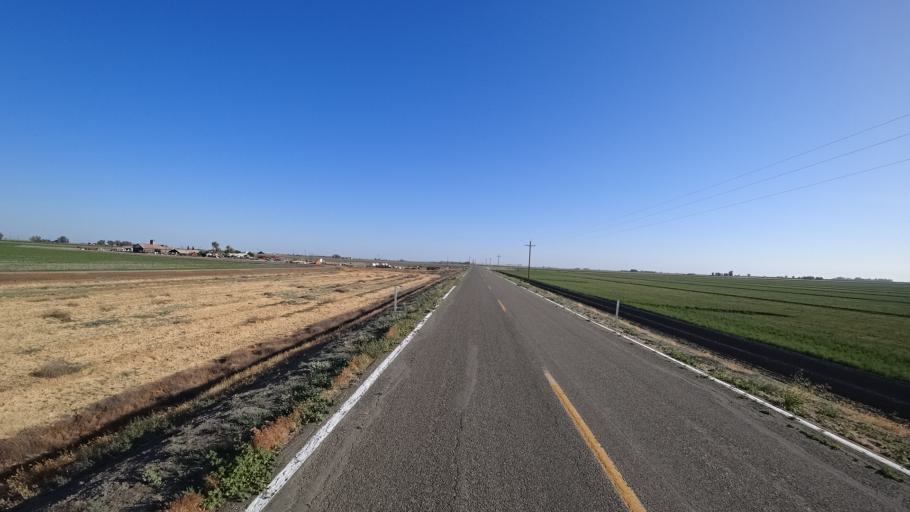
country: US
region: California
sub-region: Kings County
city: Stratford
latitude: 36.1490
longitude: -119.7981
